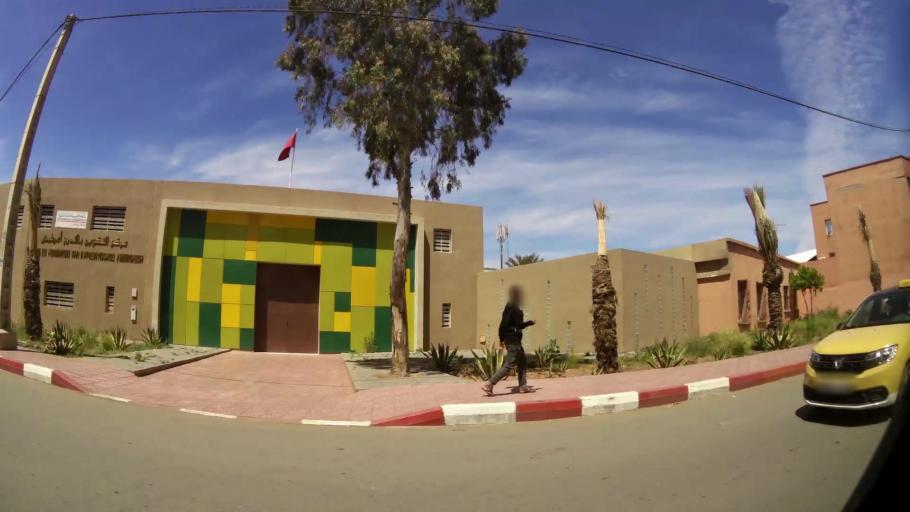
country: MA
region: Marrakech-Tensift-Al Haouz
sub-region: Marrakech
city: Marrakesh
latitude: 31.6590
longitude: -7.9922
